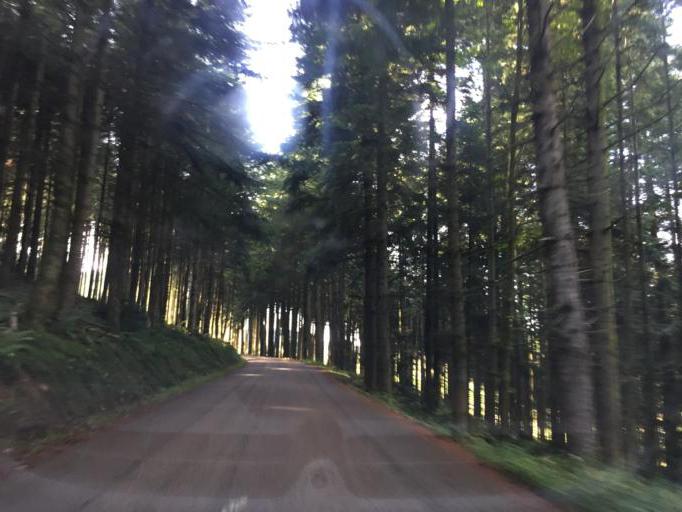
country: FR
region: Bourgogne
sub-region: Departement de Saone-et-Loire
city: Chauffailles
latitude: 46.2013
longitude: 4.3989
